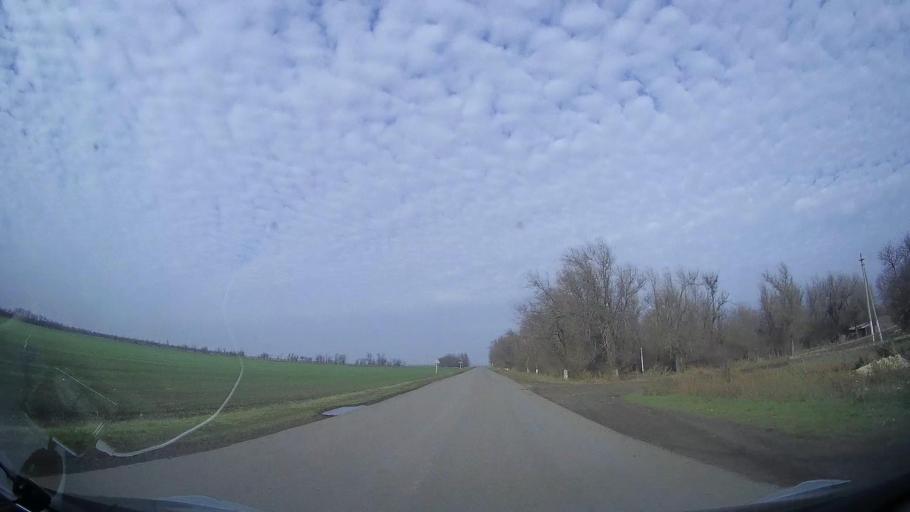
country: RU
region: Rostov
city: Gigant
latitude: 46.9252
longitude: 41.2470
